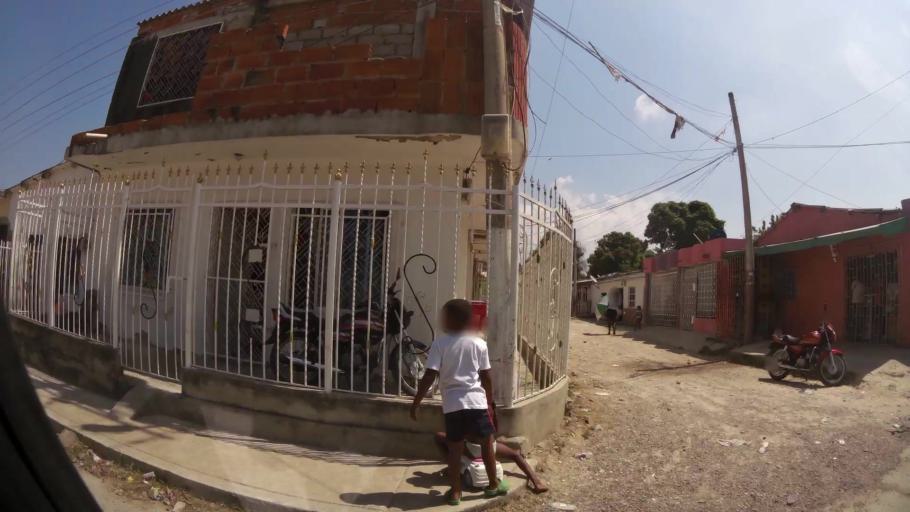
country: CO
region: Bolivar
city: Cartagena
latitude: 10.4042
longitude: -75.4907
